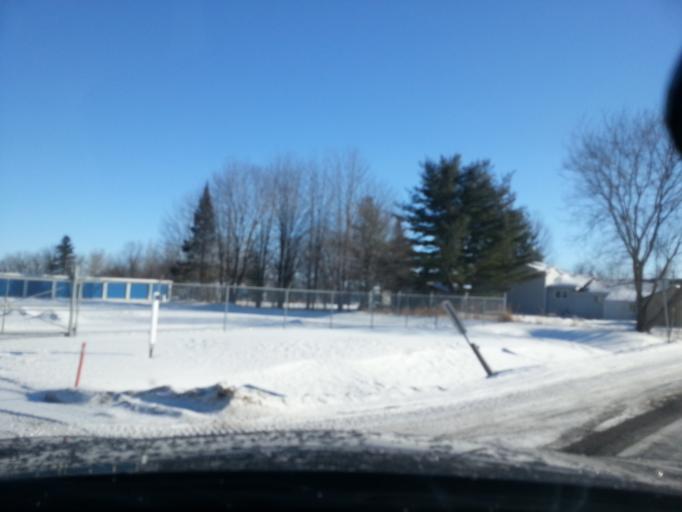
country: CA
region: Ontario
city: Bourget
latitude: 45.2561
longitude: -75.3972
